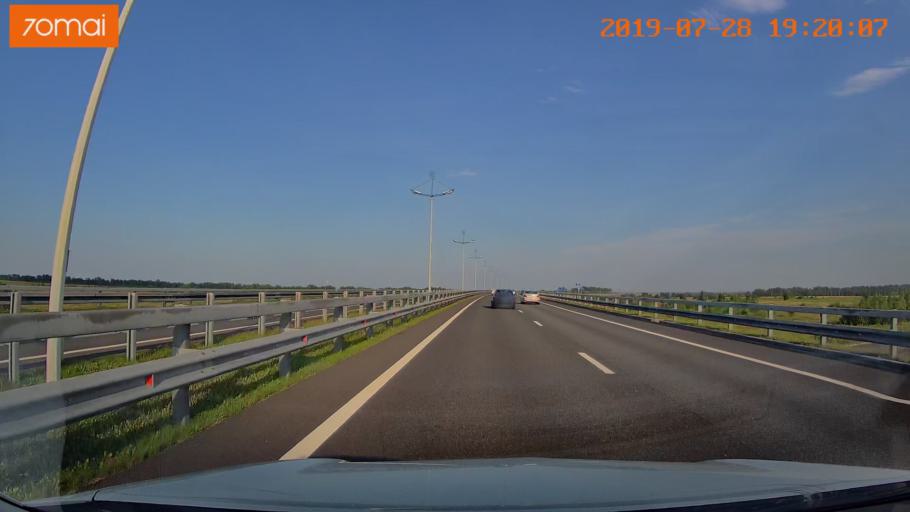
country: RU
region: Kaliningrad
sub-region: Zelenogradskiy Rayon
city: Zelenogradsk
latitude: 54.9176
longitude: 20.4779
